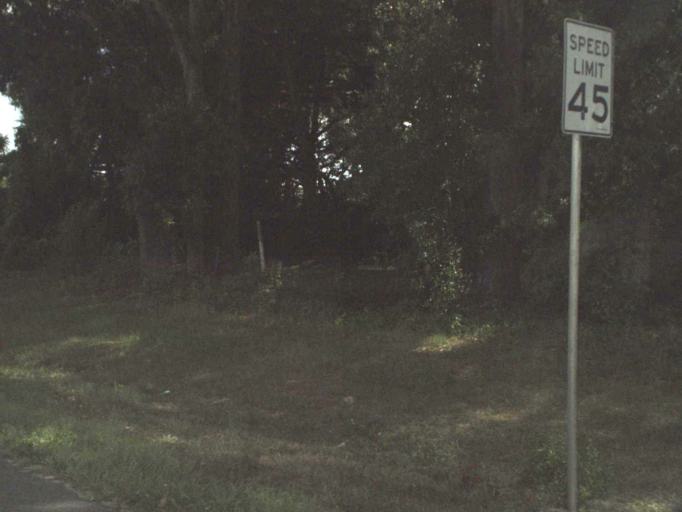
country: US
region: Florida
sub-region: Marion County
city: Belleview
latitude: 29.0742
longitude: -82.0536
